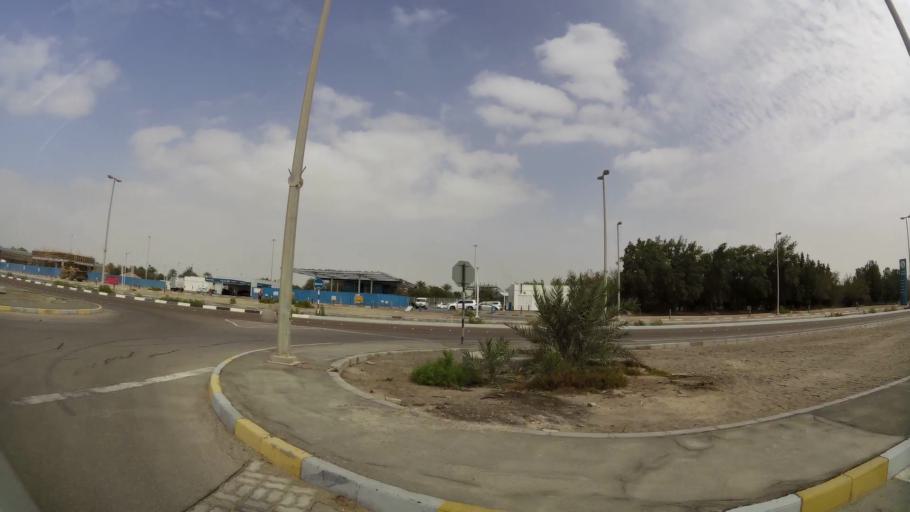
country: AE
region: Abu Dhabi
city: Abu Dhabi
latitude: 24.3948
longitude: 54.5087
